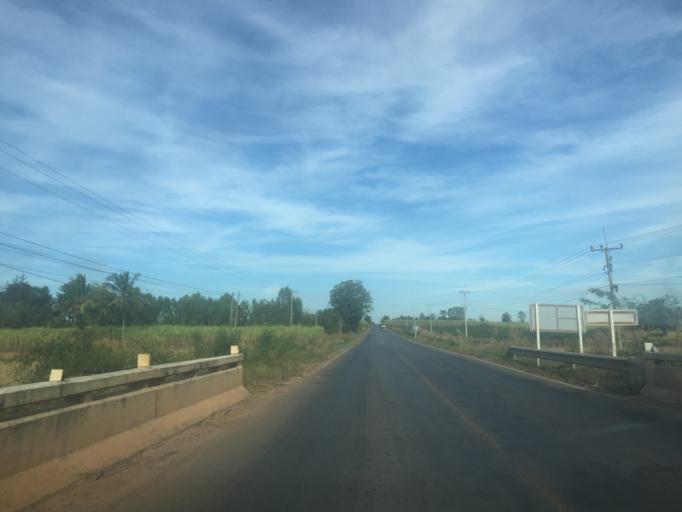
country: TH
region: Changwat Udon Thani
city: Si That
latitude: 16.9899
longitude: 103.1532
